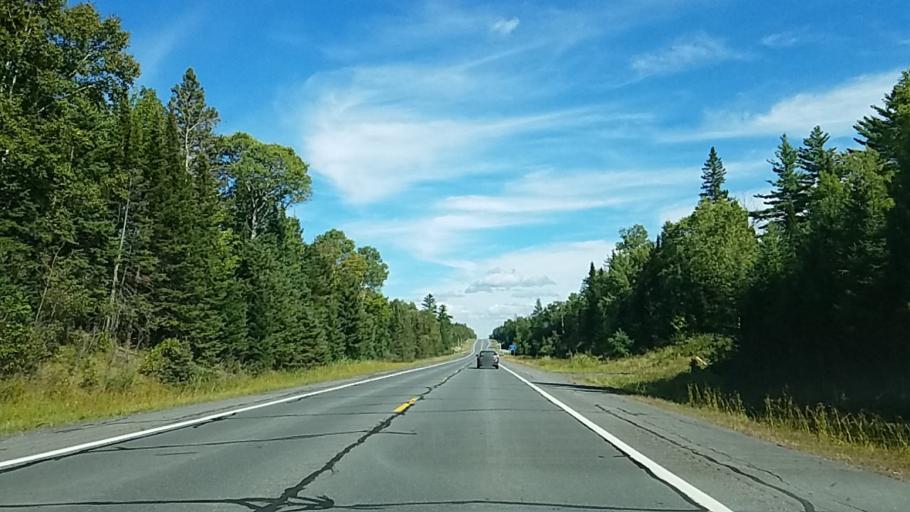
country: US
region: Michigan
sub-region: Baraga County
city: L'Anse
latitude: 46.5759
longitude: -88.3453
